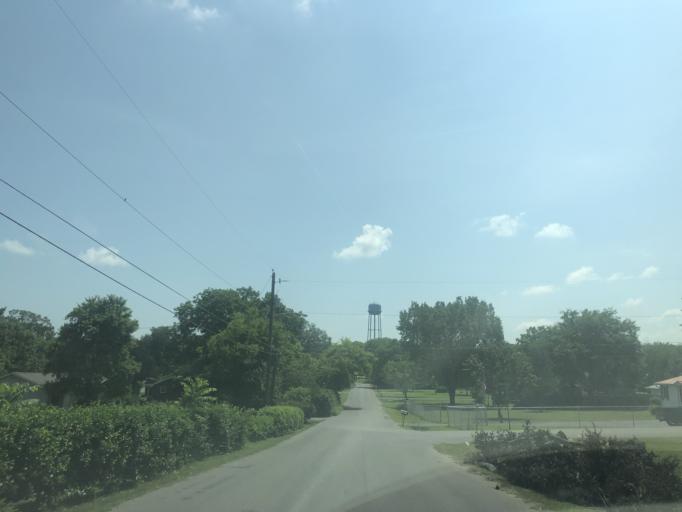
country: US
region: Tennessee
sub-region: Rutherford County
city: La Vergne
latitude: 36.0138
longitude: -86.5872
